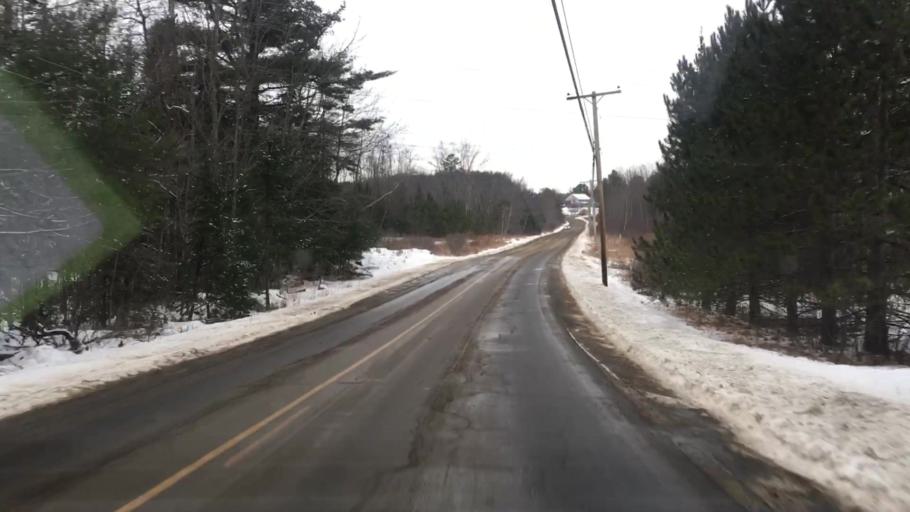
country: US
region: Maine
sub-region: Lincoln County
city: Whitefield
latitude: 44.2314
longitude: -69.6154
